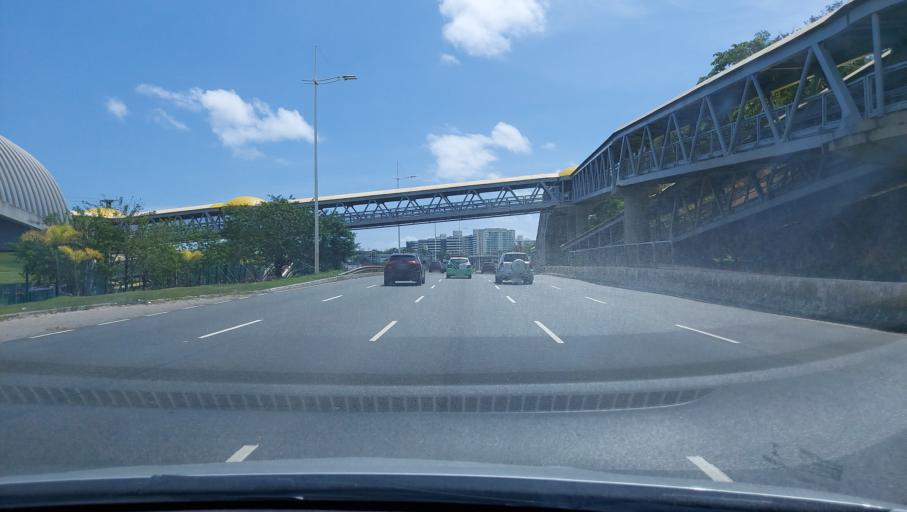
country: BR
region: Bahia
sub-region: Lauro De Freitas
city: Lauro de Freitas
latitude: -12.9346
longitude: -38.3950
